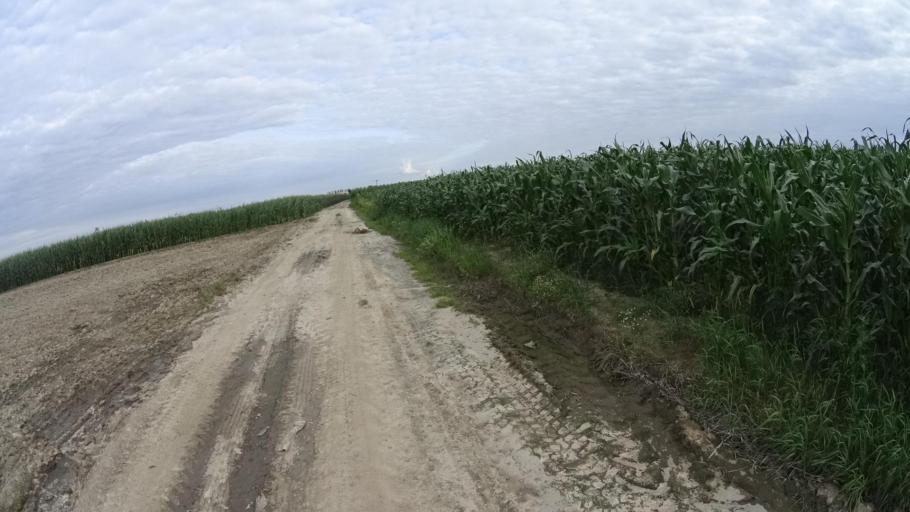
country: PL
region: Masovian Voivodeship
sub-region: Powiat warszawski zachodni
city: Babice
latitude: 52.2352
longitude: 20.8725
